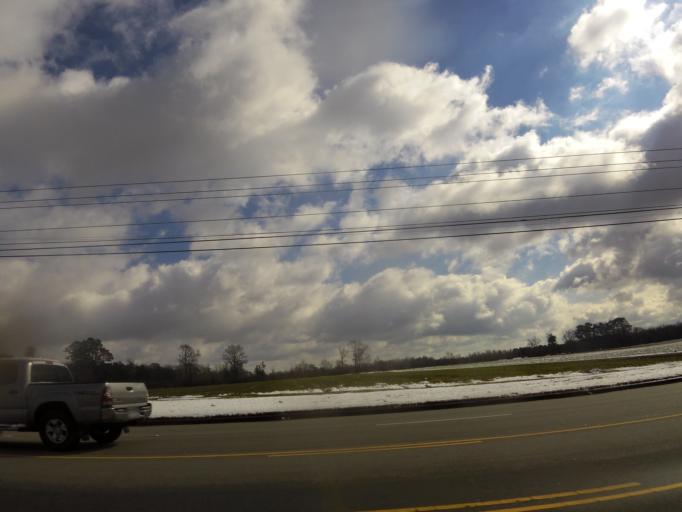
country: US
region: North Carolina
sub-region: Wilson County
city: Wilson
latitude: 35.7190
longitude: -77.9892
